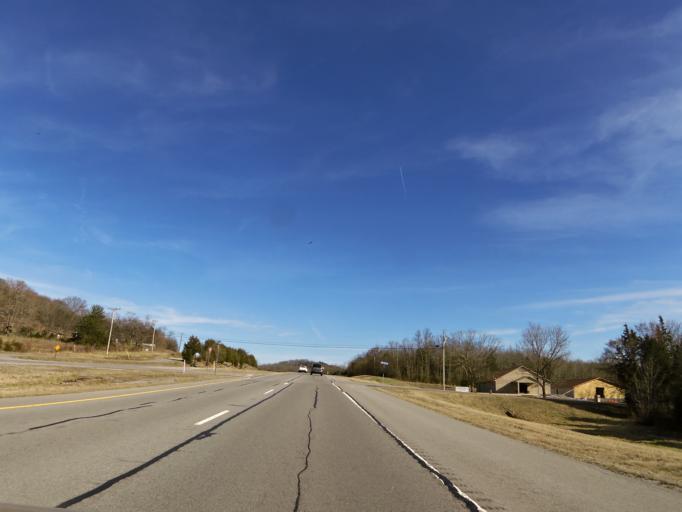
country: US
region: Tennessee
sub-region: Cannon County
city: Woodbury
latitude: 35.8106
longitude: -86.2110
